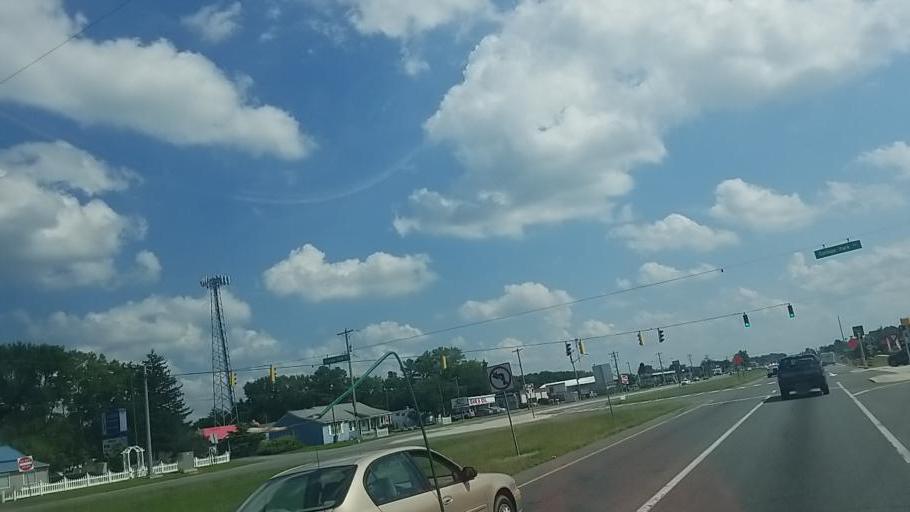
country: US
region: Delaware
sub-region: Sussex County
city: Georgetown
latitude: 38.7024
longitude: -75.4022
